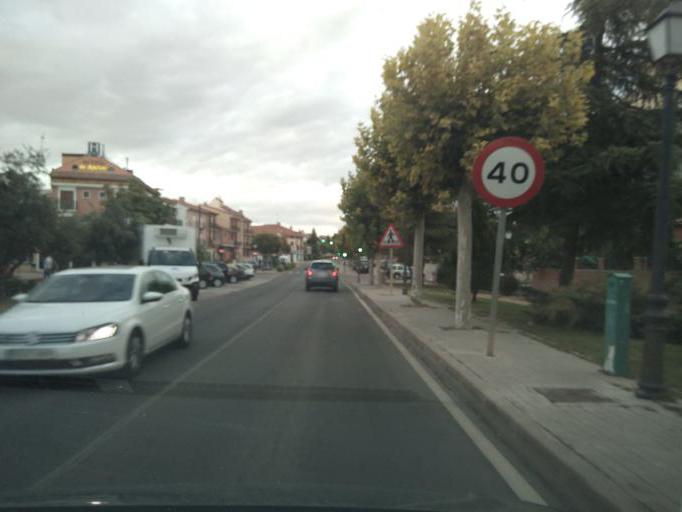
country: ES
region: Madrid
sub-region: Provincia de Madrid
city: Ajalvir
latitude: 40.5324
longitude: -3.4795
